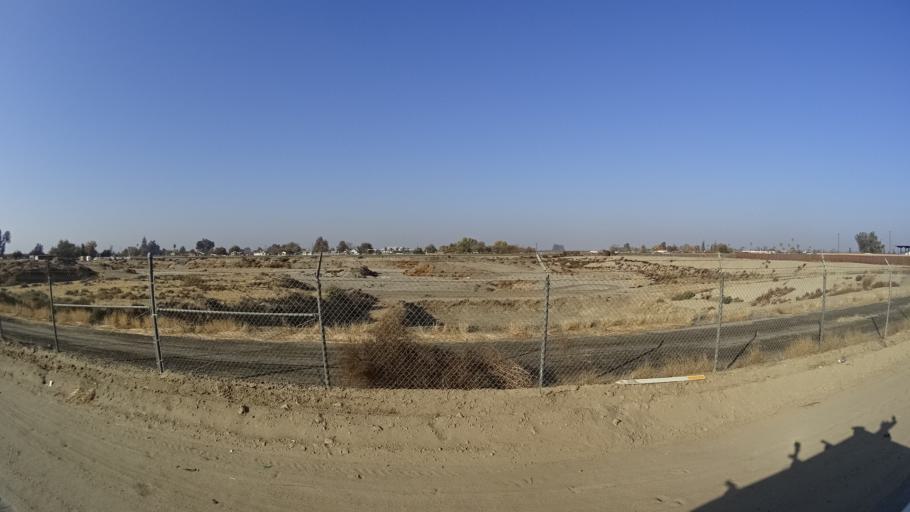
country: US
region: California
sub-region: Kern County
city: Greenfield
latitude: 35.2624
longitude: -119.0257
